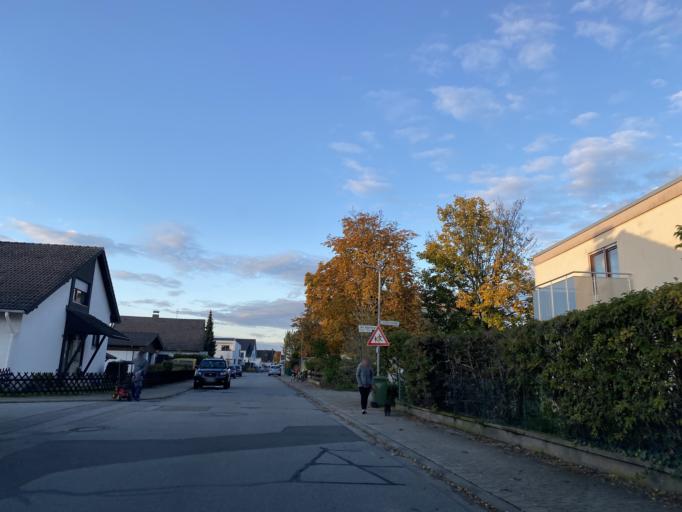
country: DE
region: Hesse
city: Zwingenberg
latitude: 49.7083
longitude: 8.6138
